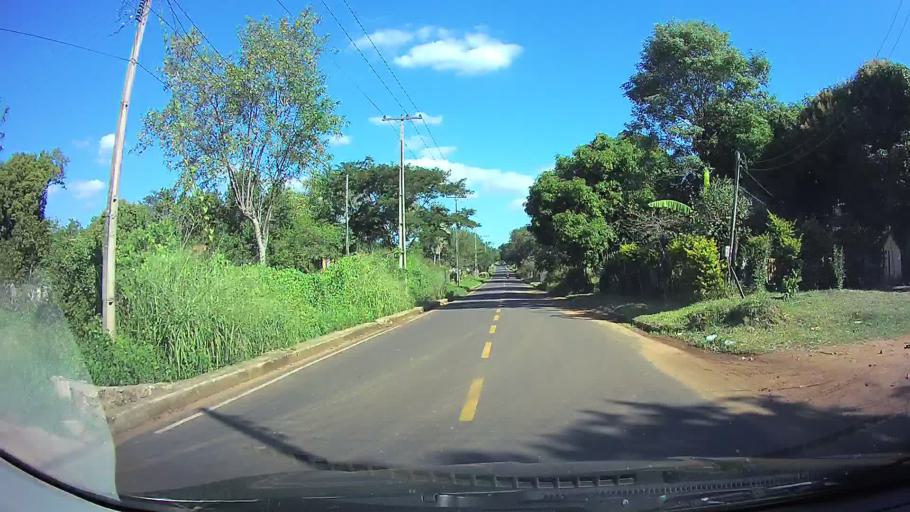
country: PY
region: Central
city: Limpio
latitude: -25.1970
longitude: -57.4775
